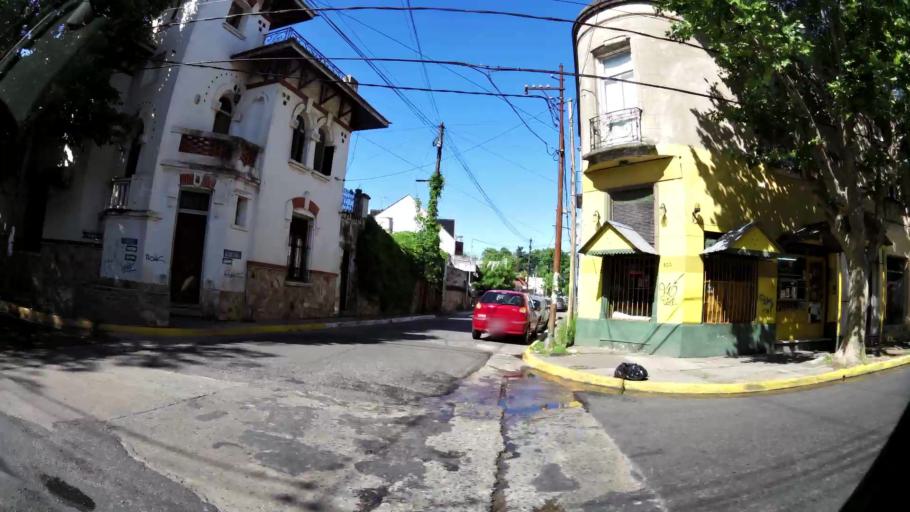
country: AR
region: Buenos Aires
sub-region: Partido de Quilmes
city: Quilmes
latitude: -34.7065
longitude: -58.2837
